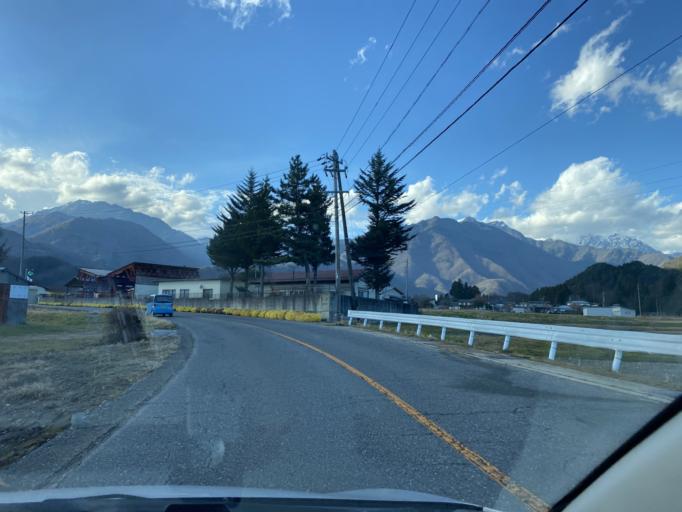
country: JP
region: Nagano
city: Omachi
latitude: 36.5277
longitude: 137.8238
